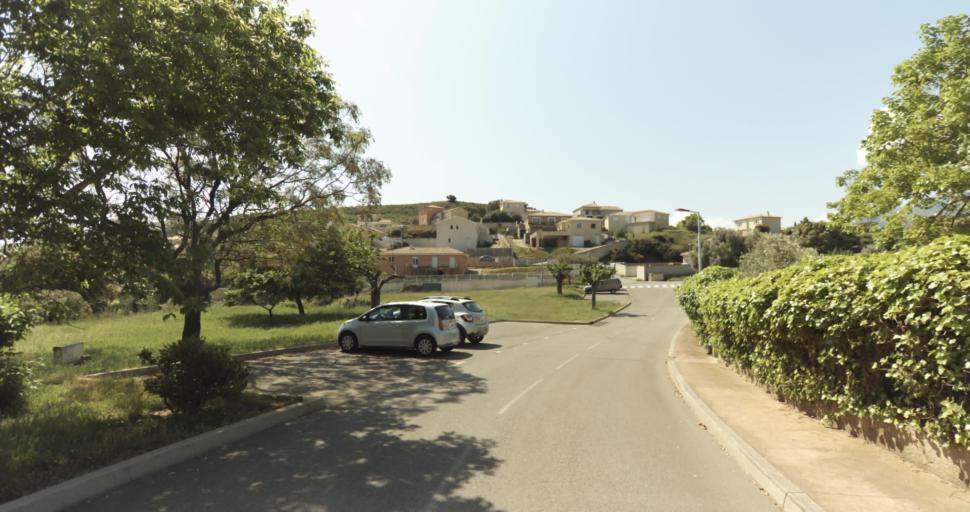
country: FR
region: Corsica
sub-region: Departement de la Haute-Corse
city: Biguglia
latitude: 42.6206
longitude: 9.4272
